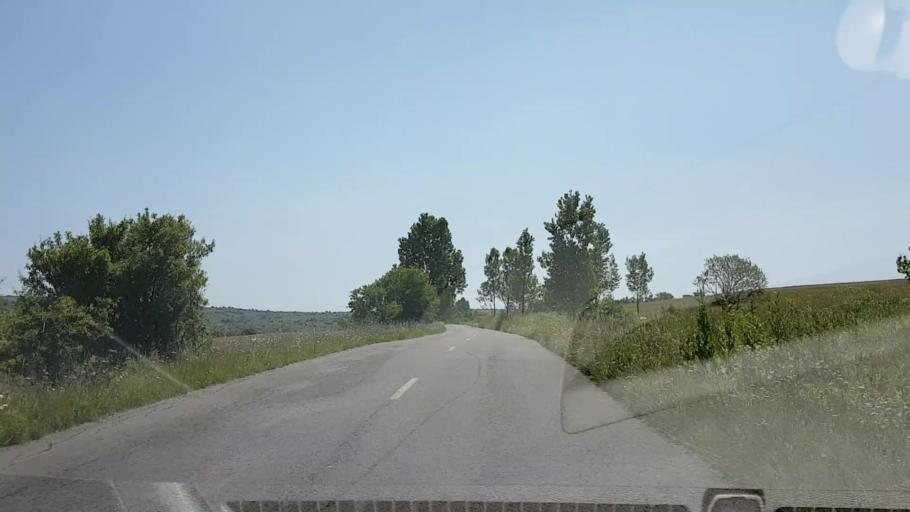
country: RO
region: Sibiu
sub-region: Comuna Merghindeal
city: Merghindeal
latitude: 45.9565
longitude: 24.7716
